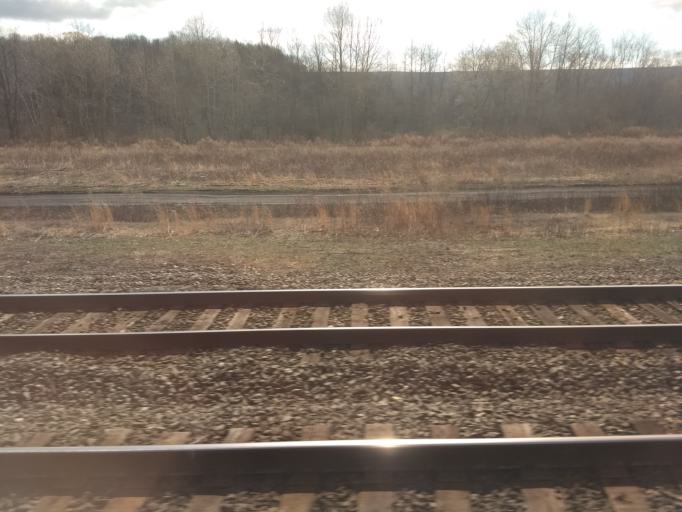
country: US
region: Pennsylvania
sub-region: Blair County
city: Greenwood
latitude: 40.5725
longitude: -78.3554
